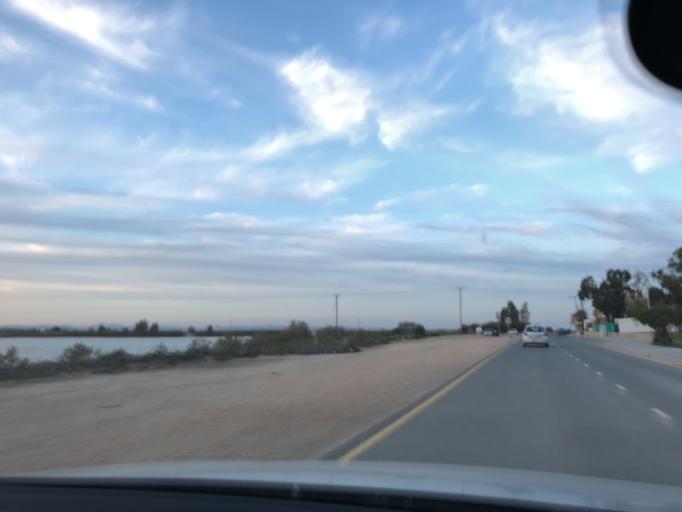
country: CY
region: Larnaka
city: Meneou
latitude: 34.8434
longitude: 33.6144
